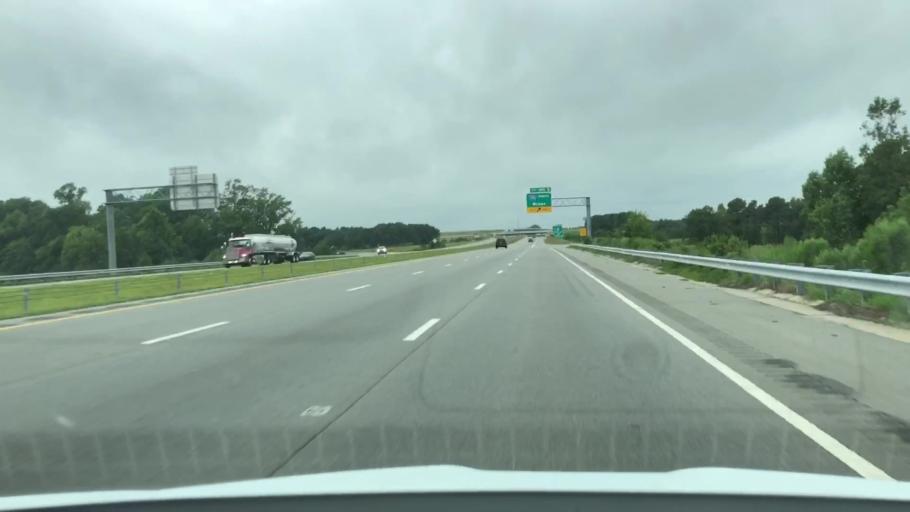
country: US
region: North Carolina
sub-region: Wayne County
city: Goldsboro
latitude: 35.4262
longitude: -77.9849
